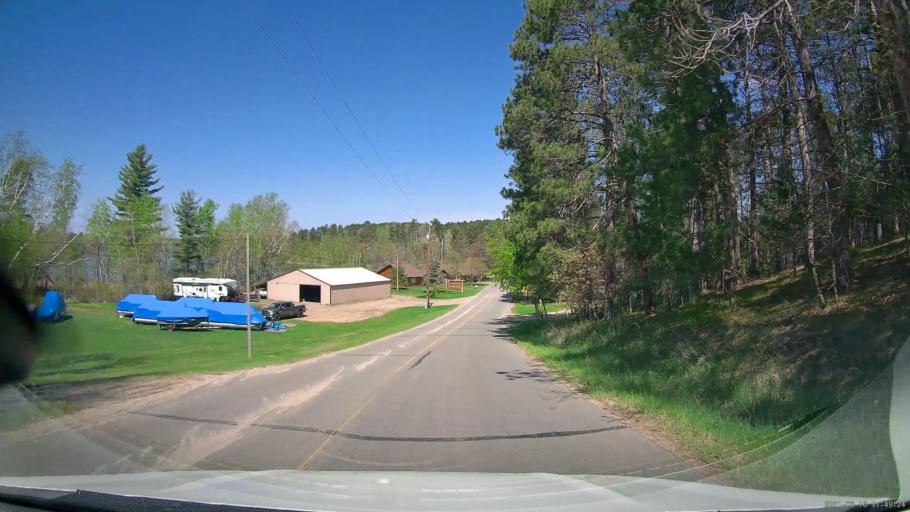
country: US
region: Minnesota
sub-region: Hubbard County
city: Park Rapids
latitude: 46.9868
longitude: -94.9516
